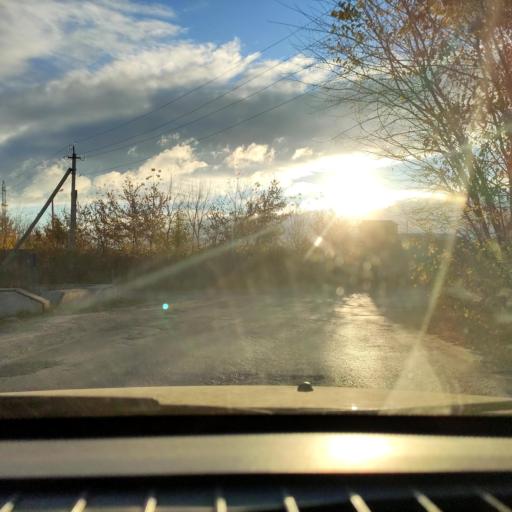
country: RU
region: Samara
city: Tol'yatti
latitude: 53.5751
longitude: 49.2880
